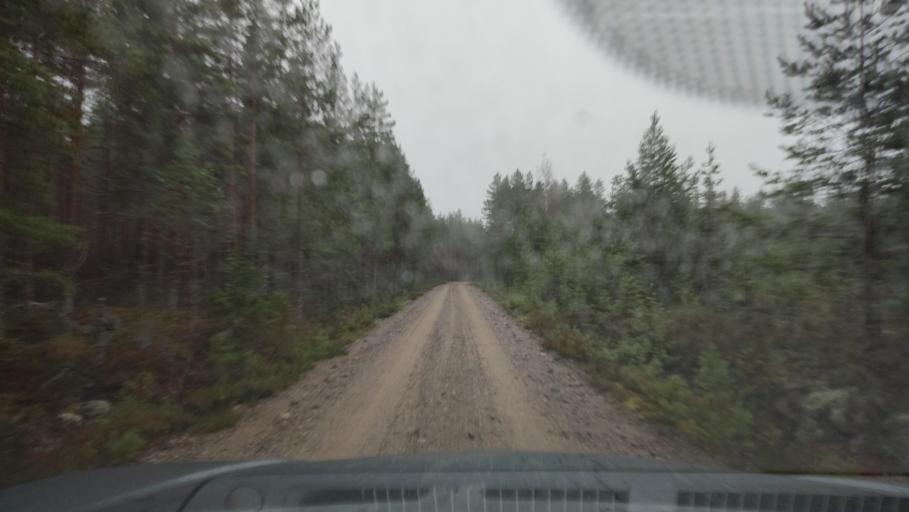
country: FI
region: Southern Ostrobothnia
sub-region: Suupohja
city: Karijoki
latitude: 62.1924
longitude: 21.7440
